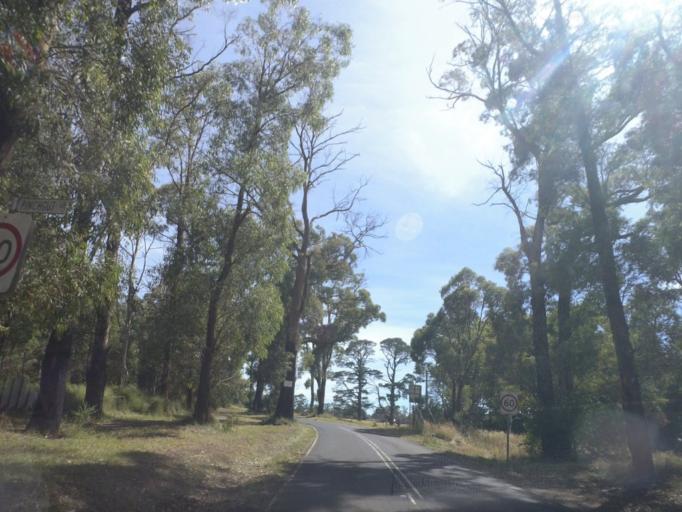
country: AU
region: Victoria
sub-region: Nillumbik
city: Saint Andrews
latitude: -37.5373
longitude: 145.3399
